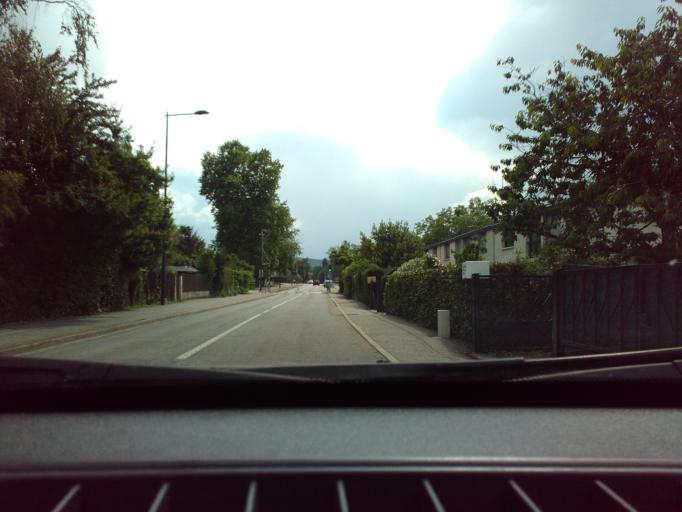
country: FR
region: Rhone-Alpes
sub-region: Departement de l'Isere
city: Saint-Martin-d'Heres
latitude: 45.1670
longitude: 5.7673
